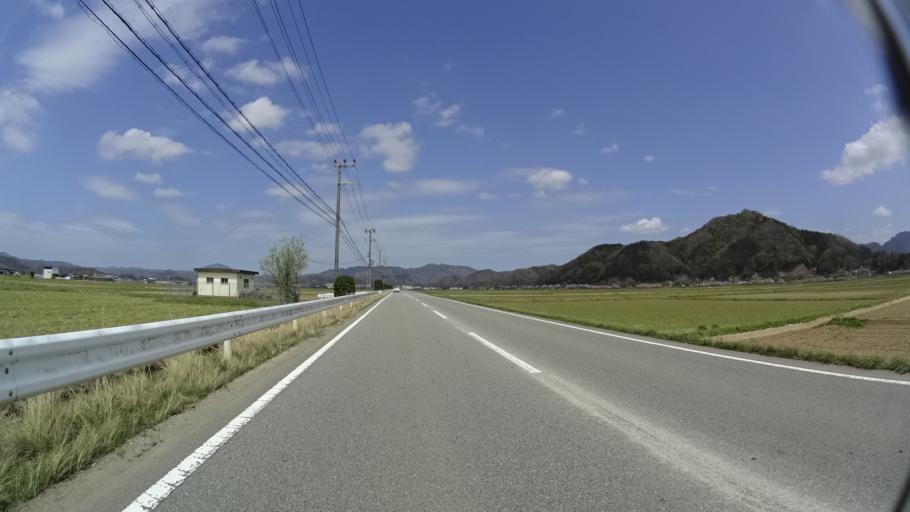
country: JP
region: Hyogo
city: Toyooka
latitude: 35.5135
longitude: 134.8400
